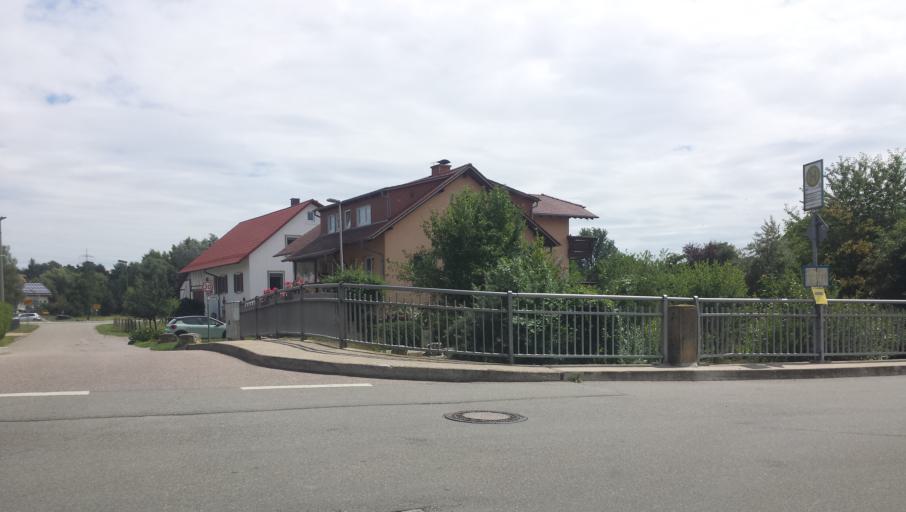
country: DE
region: Baden-Wuerttemberg
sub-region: Karlsruhe Region
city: Neidenstein
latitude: 49.3156
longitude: 8.8883
